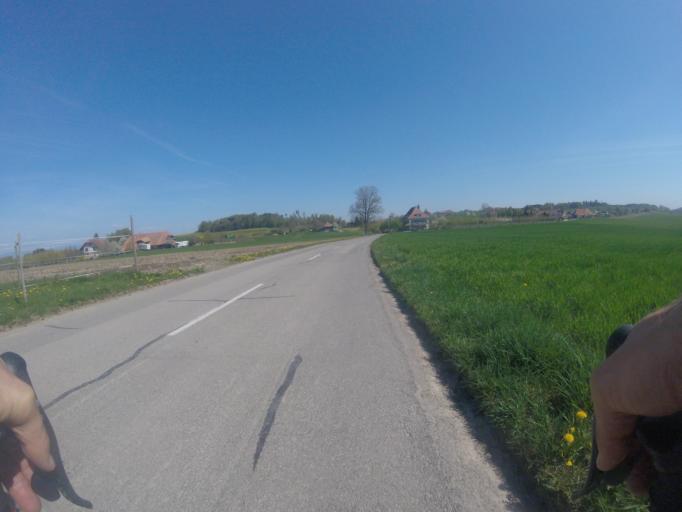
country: CH
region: Bern
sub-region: Bern-Mittelland District
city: Laupen
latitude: 46.9028
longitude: 7.2714
